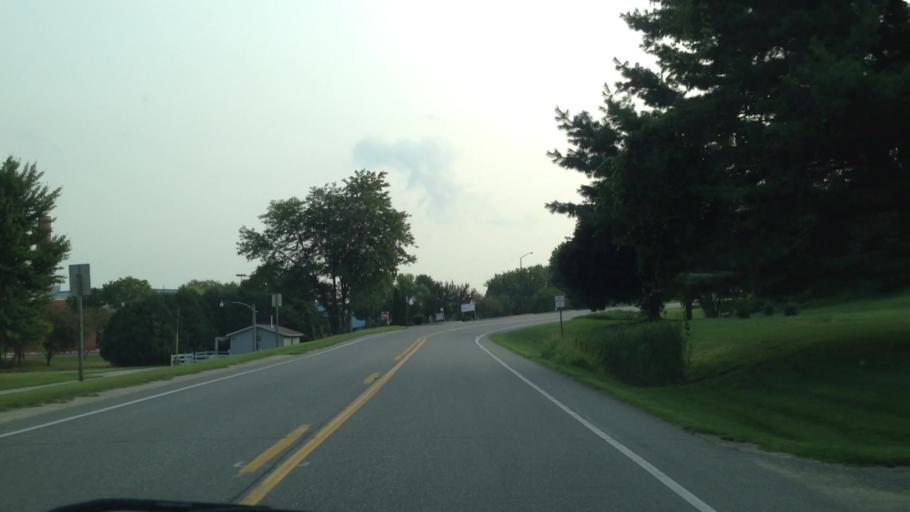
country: US
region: Iowa
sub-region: Benton County
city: Walford
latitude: 41.7948
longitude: -91.8985
